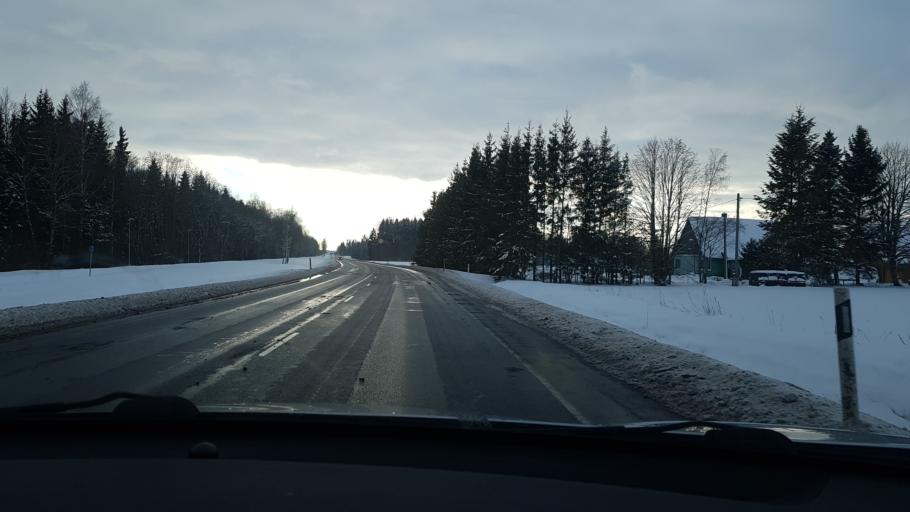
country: EE
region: Jaervamaa
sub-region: Paide linn
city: Paide
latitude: 58.9356
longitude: 25.6350
